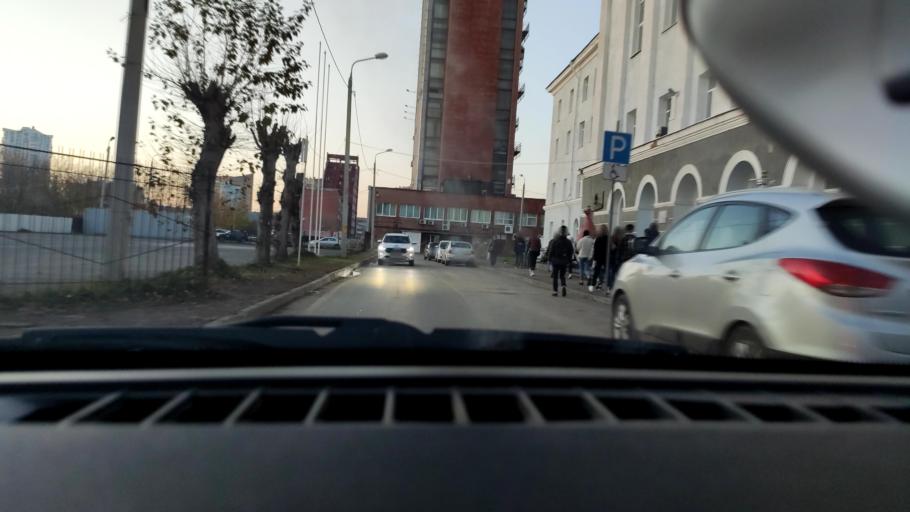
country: RU
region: Perm
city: Perm
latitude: 58.0174
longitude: 56.2743
